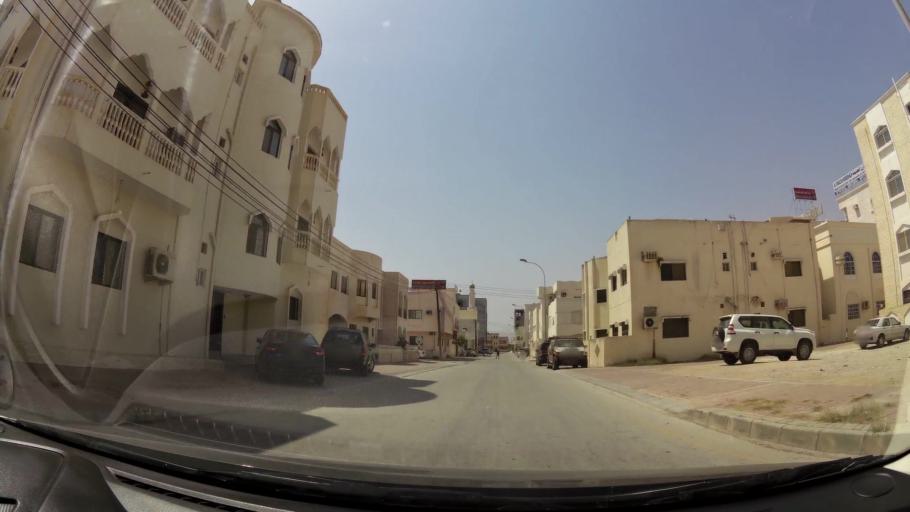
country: OM
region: Zufar
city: Salalah
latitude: 17.0195
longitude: 54.0879
